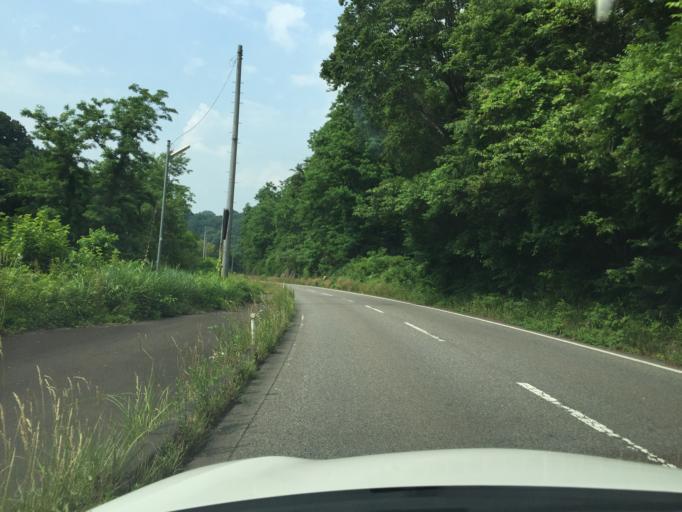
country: JP
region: Fukushima
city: Sukagawa
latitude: 37.3061
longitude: 140.4412
